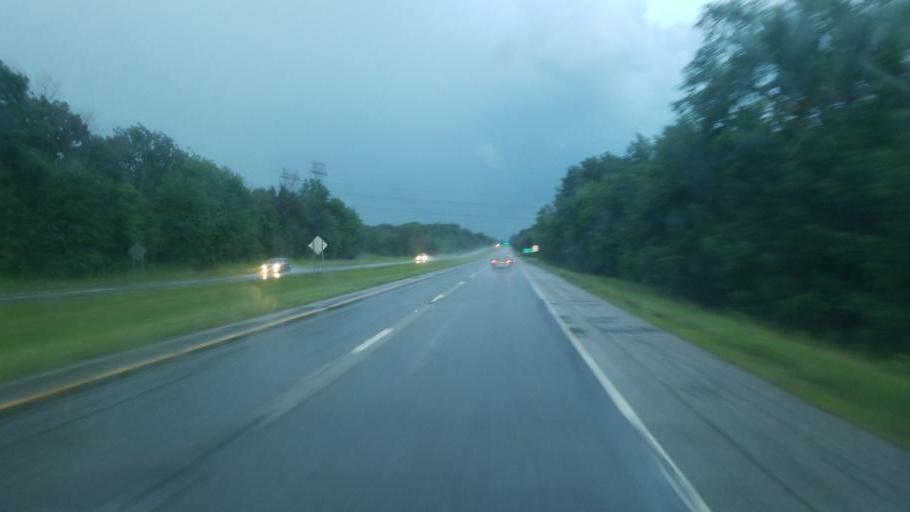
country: US
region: Ohio
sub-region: Wayne County
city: Doylestown
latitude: 40.9699
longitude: -81.6612
